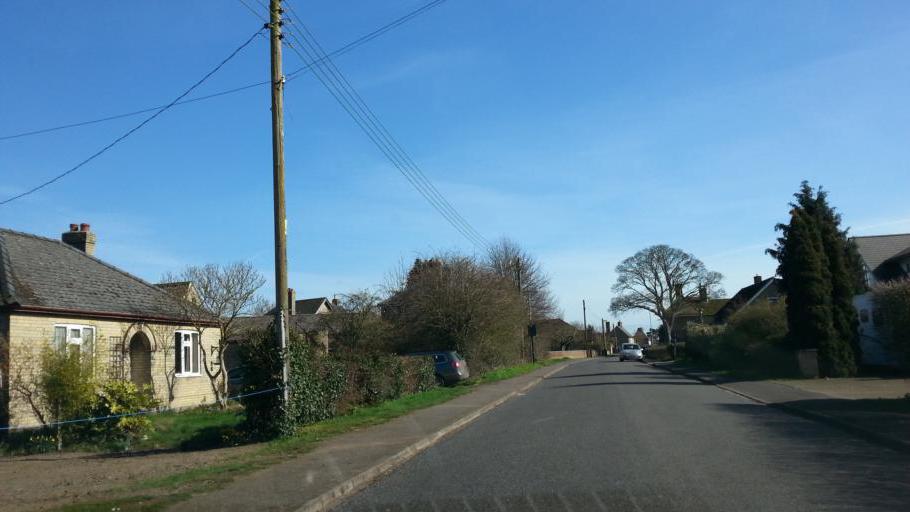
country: GB
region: England
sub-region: Cambridgeshire
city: Swavesey
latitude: 52.3116
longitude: 0.0126
